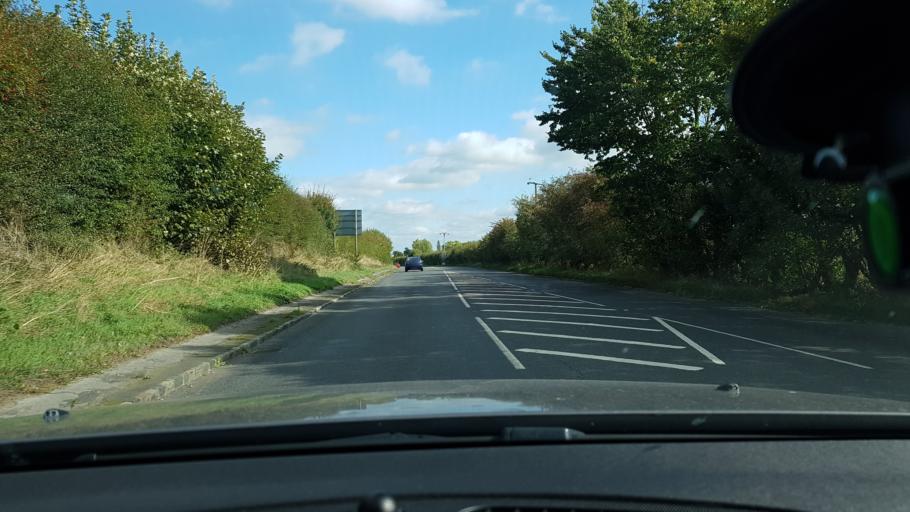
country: GB
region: England
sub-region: West Berkshire
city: Hungerford
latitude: 51.4156
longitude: -1.4925
